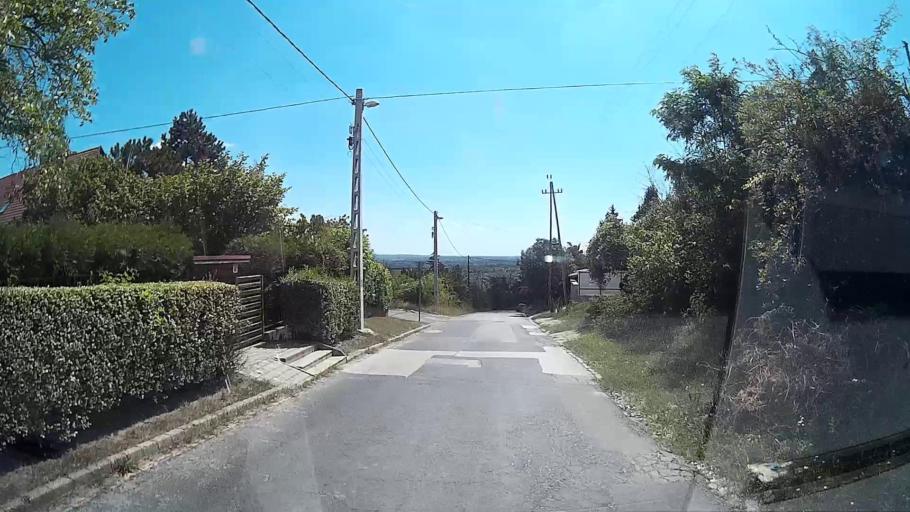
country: HU
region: Pest
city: Leanyfalu
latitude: 47.6951
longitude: 19.0824
